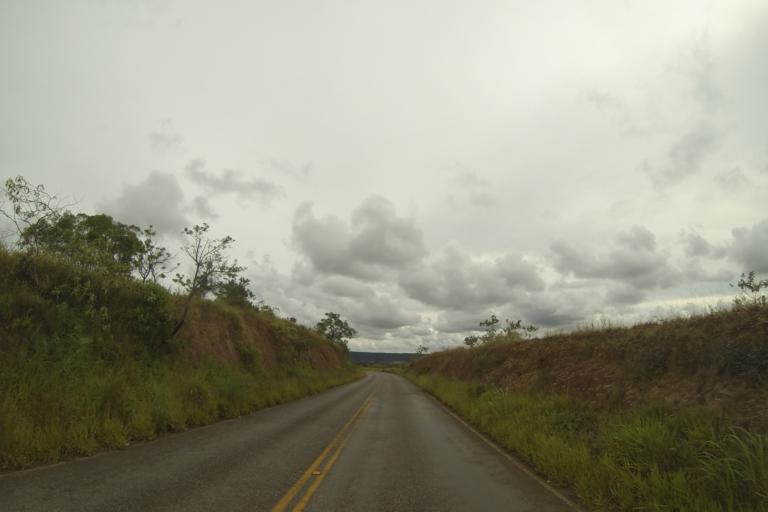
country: BR
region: Minas Gerais
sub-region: Ibia
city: Ibia
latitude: -19.6845
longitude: -46.4442
